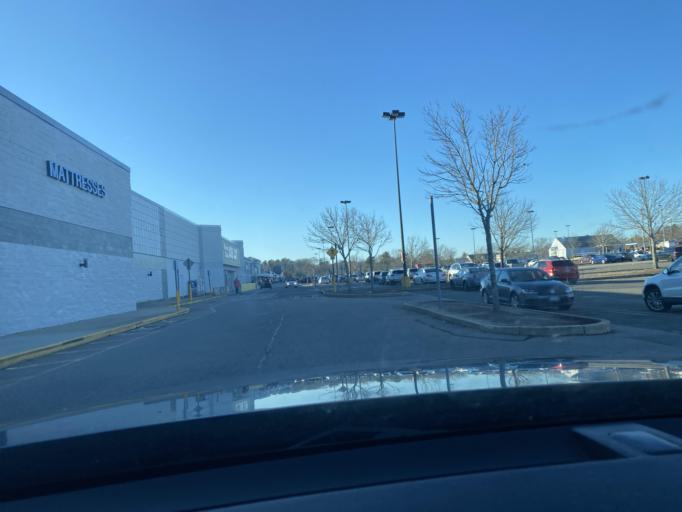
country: US
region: Massachusetts
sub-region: Plymouth County
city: Onset
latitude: 41.7581
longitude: -70.6629
